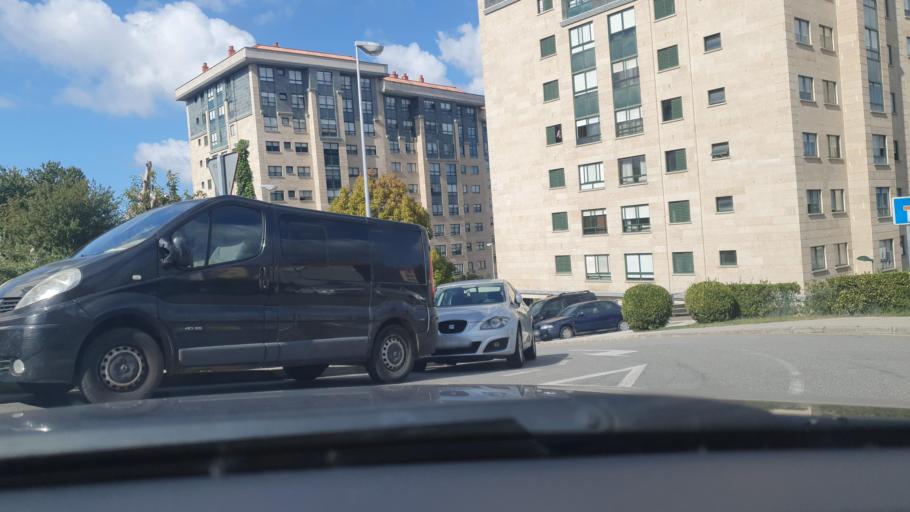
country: ES
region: Galicia
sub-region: Provincia de Pontevedra
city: Vigo
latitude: 42.2224
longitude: -8.7574
